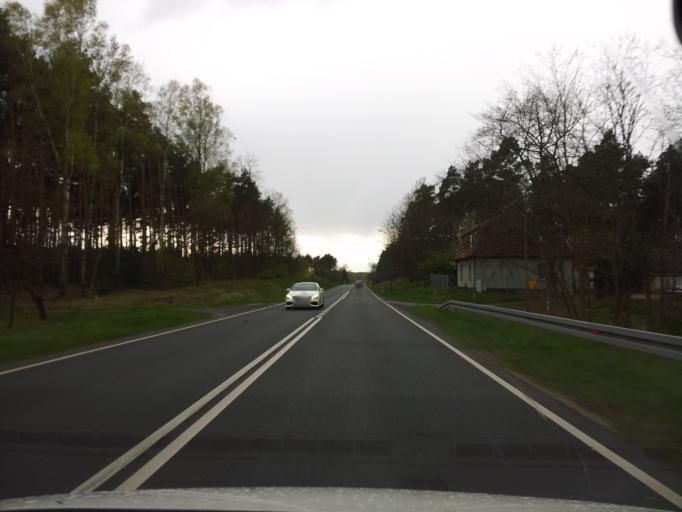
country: PL
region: Lubusz
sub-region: Powiat krosnienski
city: Bobrowice
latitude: 51.9979
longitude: 15.0291
